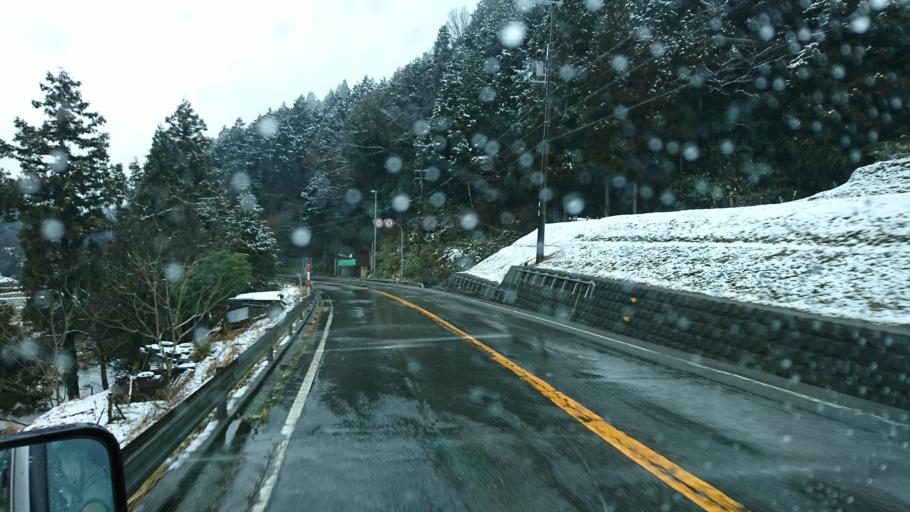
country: JP
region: Tottori
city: Tottori
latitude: 35.5382
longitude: 134.5107
